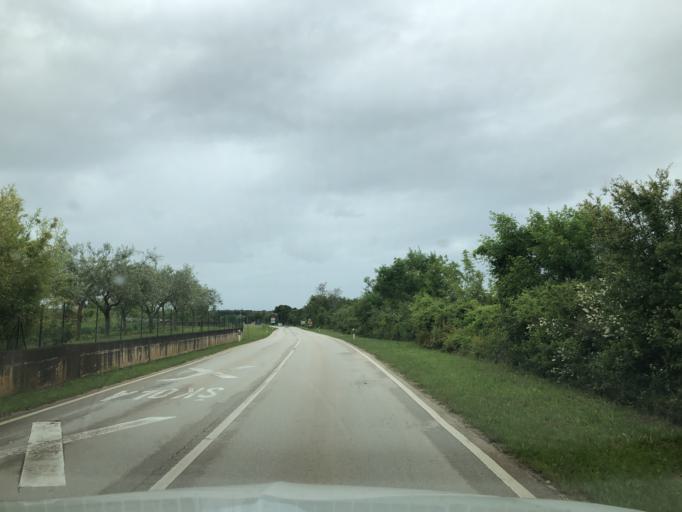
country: HR
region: Istarska
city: Umag
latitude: 45.4496
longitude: 13.5718
